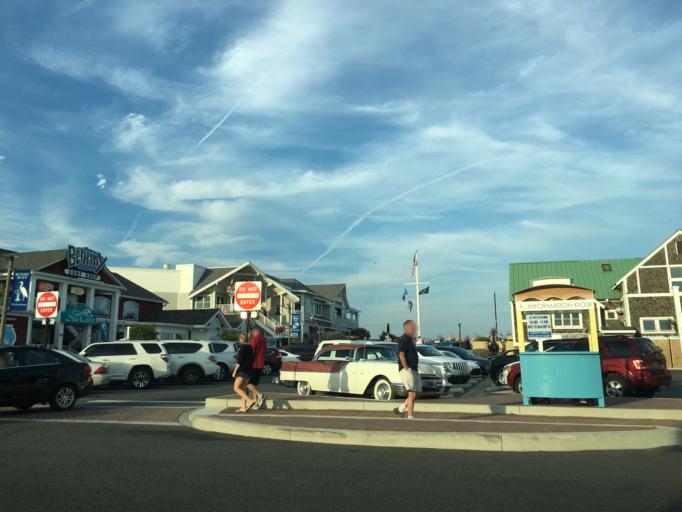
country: US
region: Delaware
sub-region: Sussex County
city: Bethany Beach
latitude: 38.5384
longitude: -75.0553
